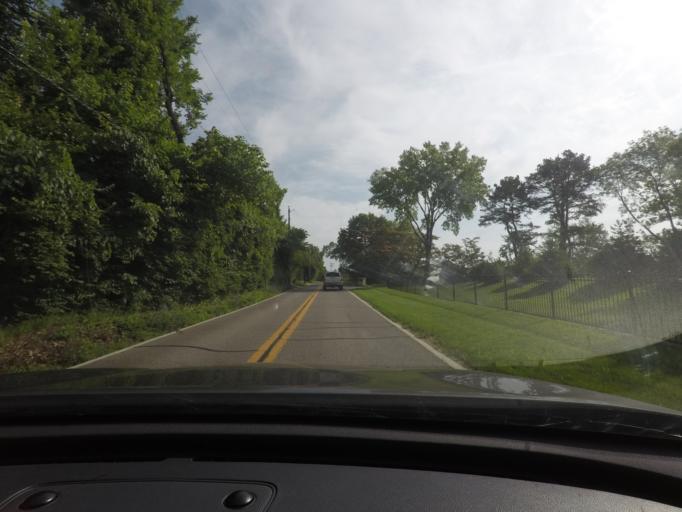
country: US
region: Missouri
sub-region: Saint Louis County
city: Town and Country
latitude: 38.6187
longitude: -90.4855
